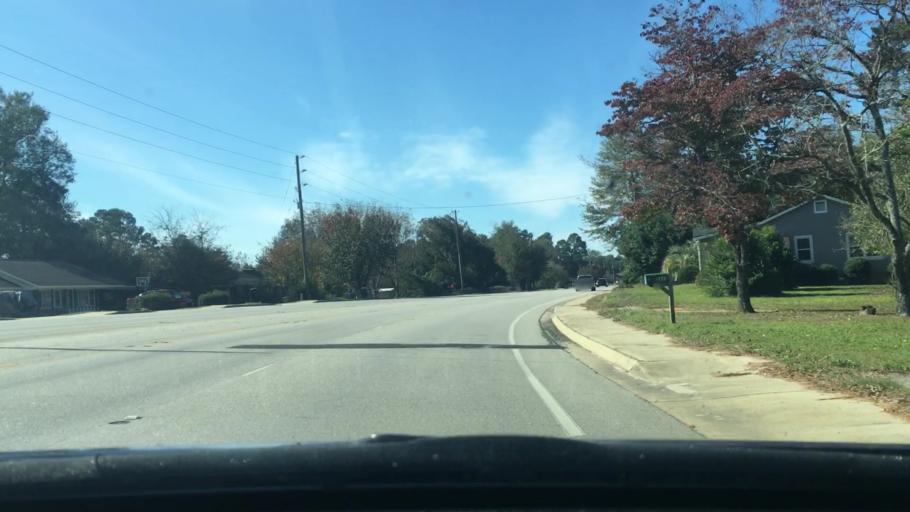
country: US
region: South Carolina
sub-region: Sumter County
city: Cane Savannah
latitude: 33.8975
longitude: -80.3993
